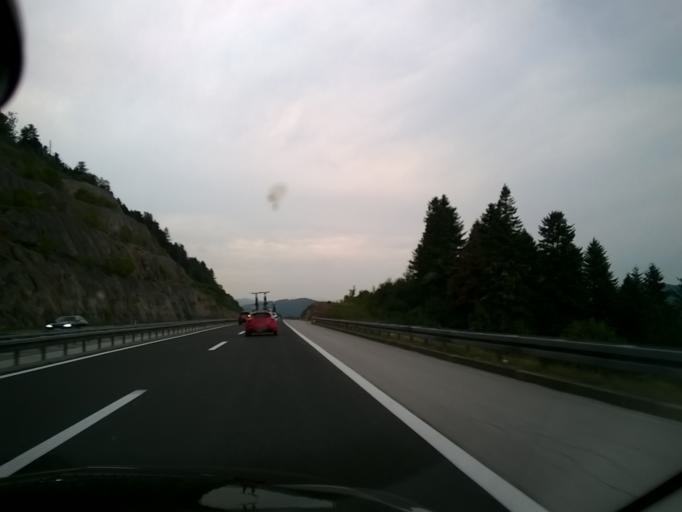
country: HR
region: Licko-Senjska
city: Otocac
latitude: 44.8515
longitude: 15.2289
